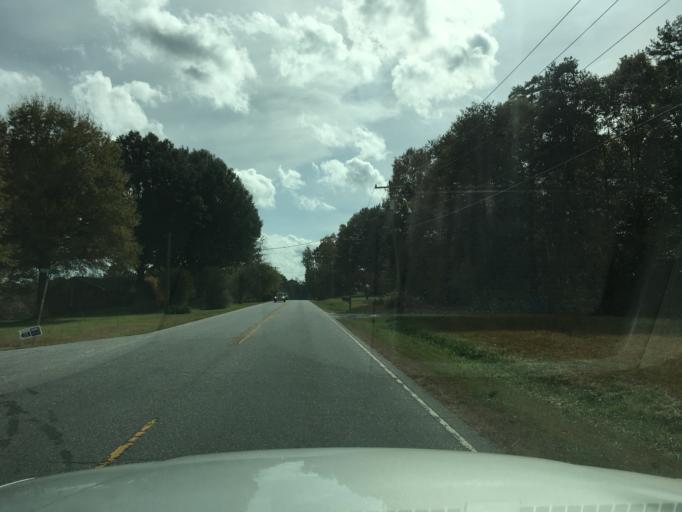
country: US
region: North Carolina
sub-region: Catawba County
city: Newton
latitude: 35.6704
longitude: -81.2730
